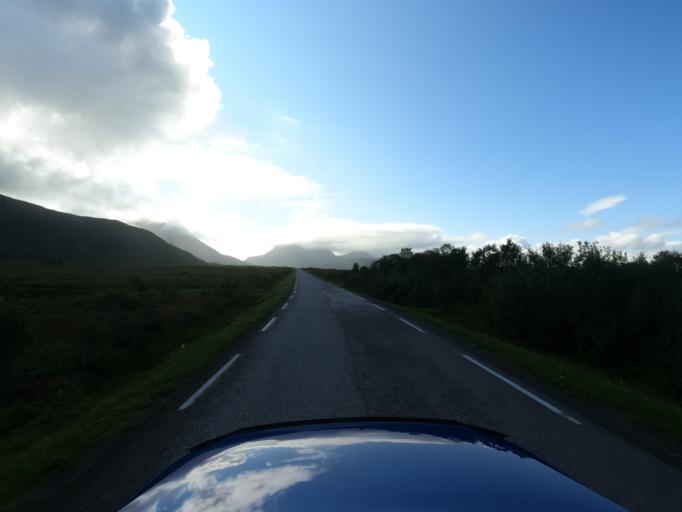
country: NO
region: Nordland
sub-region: Vagan
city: Kabelvag
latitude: 68.3080
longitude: 14.1958
